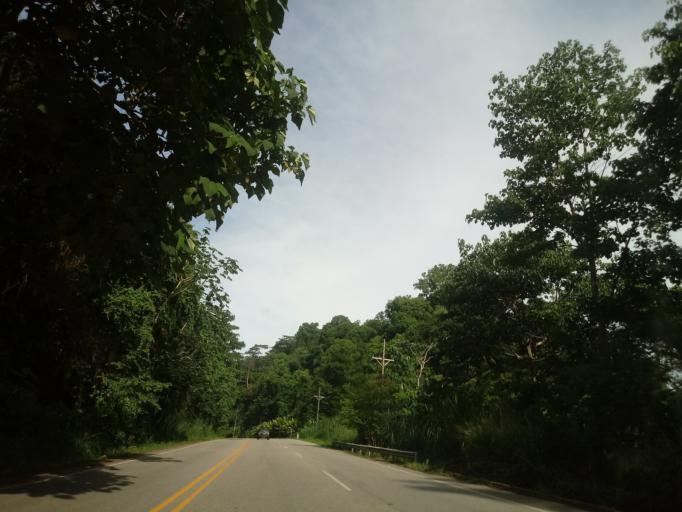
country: CR
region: San Jose
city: Daniel Flores
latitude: 9.2009
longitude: -83.7904
